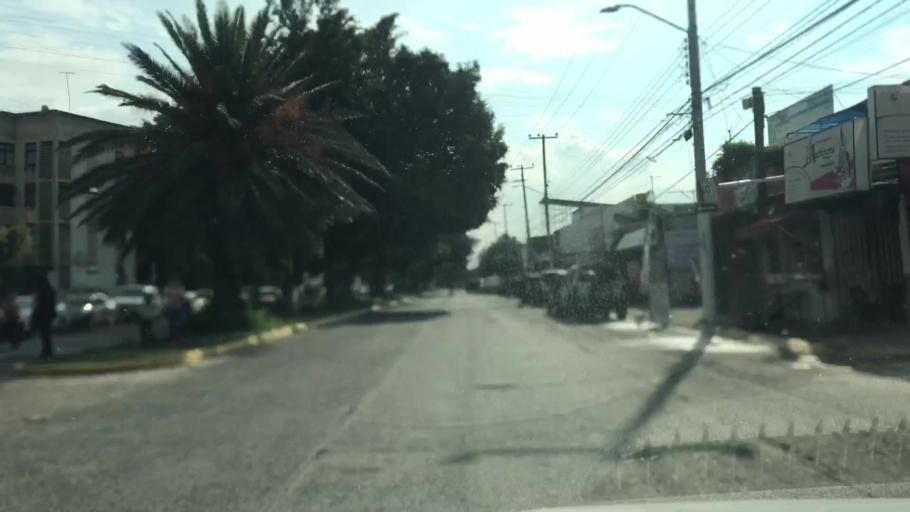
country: MX
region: Jalisco
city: Guadalajara
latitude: 20.6505
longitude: -103.4314
